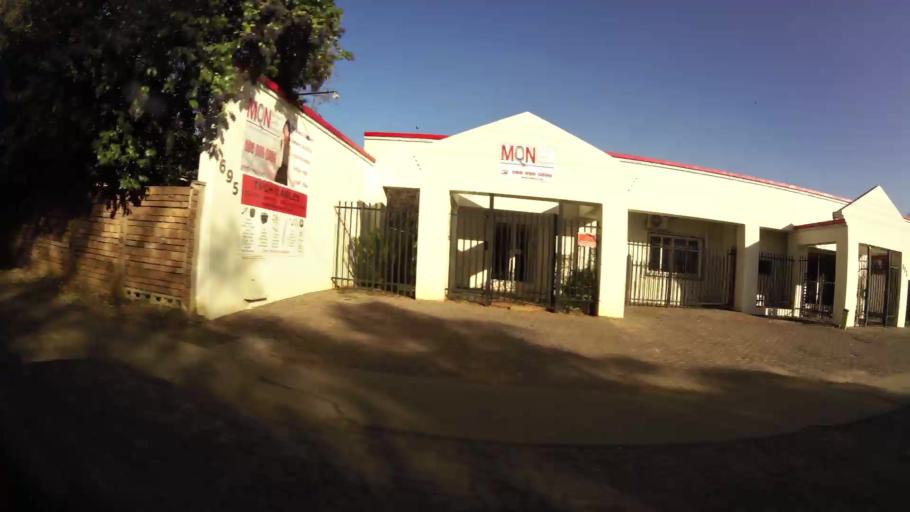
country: ZA
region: Gauteng
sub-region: City of Tshwane Metropolitan Municipality
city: Pretoria
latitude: -25.7171
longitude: 28.2146
